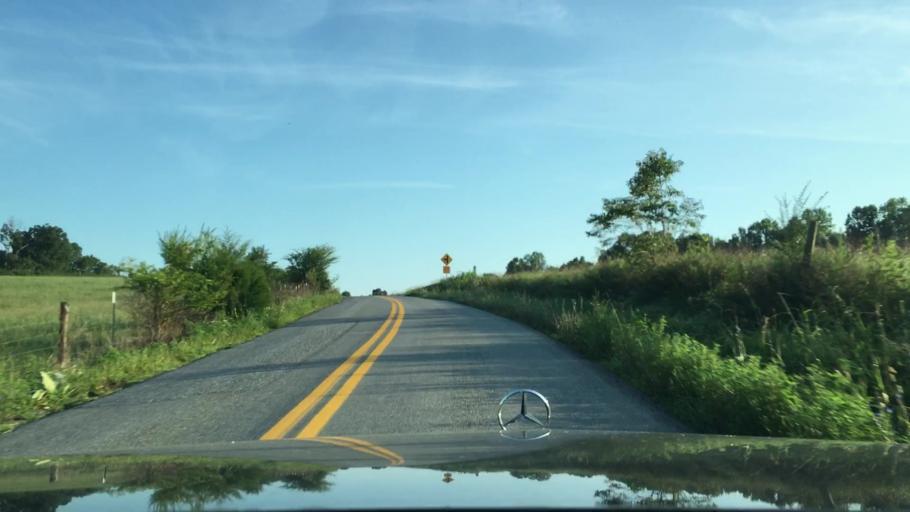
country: US
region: Virginia
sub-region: Campbell County
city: Timberlake
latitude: 37.2861
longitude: -79.2721
